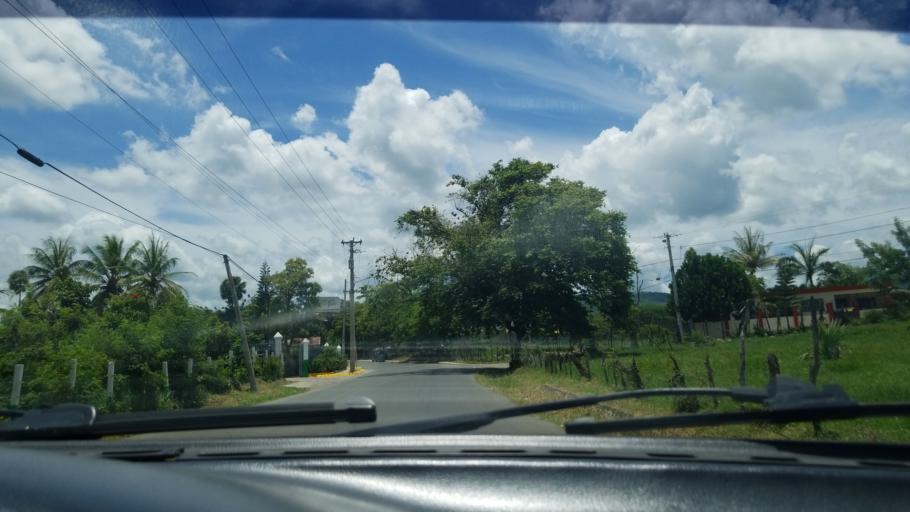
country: DO
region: Santiago
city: Santiago de los Caballeros
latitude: 19.4897
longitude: -70.6776
